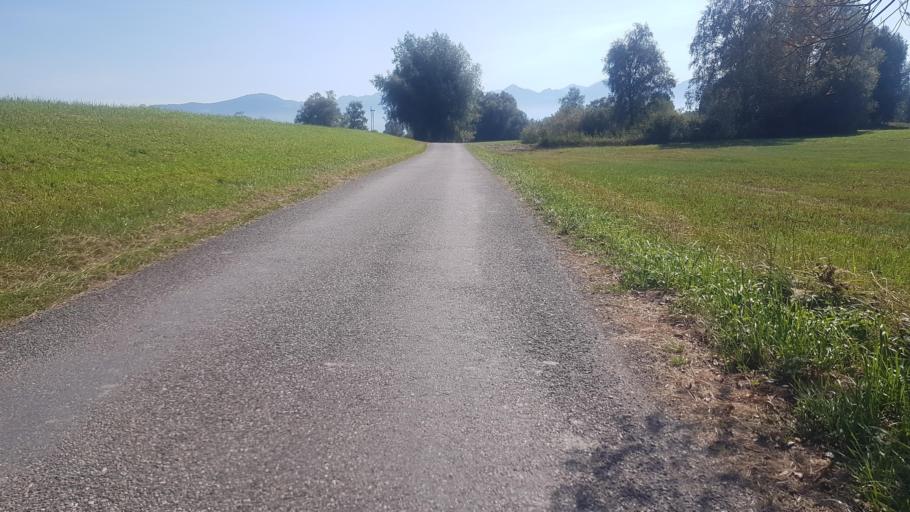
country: AT
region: Vorarlberg
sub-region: Politischer Bezirk Bregenz
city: Fussach
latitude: 47.4879
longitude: 9.6460
